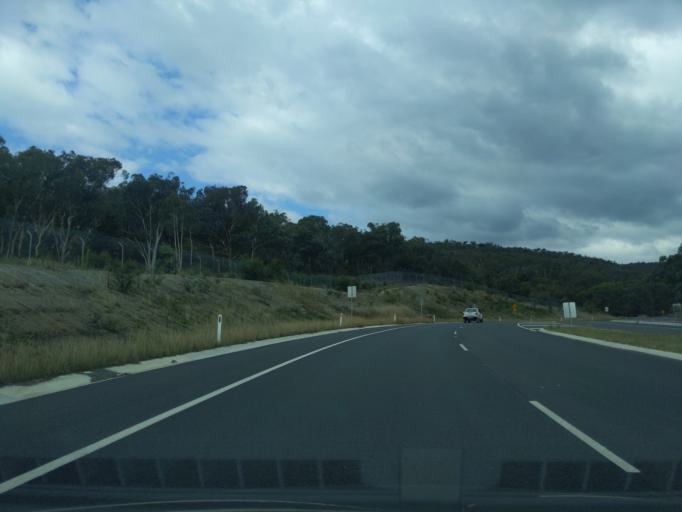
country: AU
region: New South Wales
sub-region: Queanbeyan
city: Queanbeyan
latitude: -35.3531
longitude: 149.2524
